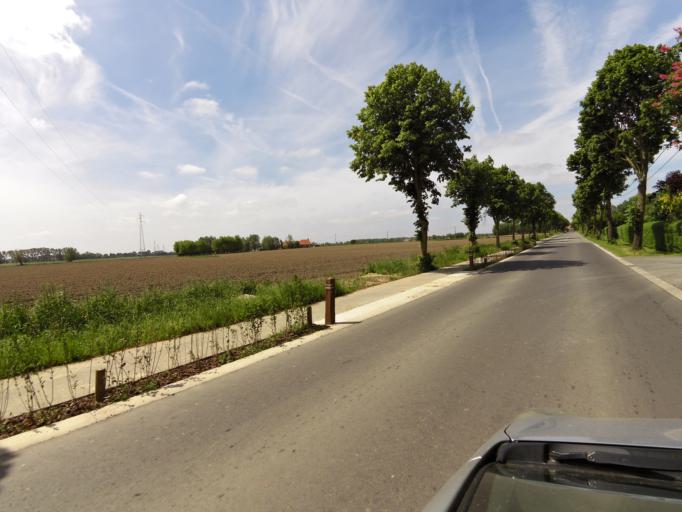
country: BE
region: Flanders
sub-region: Provincie West-Vlaanderen
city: Diksmuide
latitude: 50.9602
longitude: 2.8431
